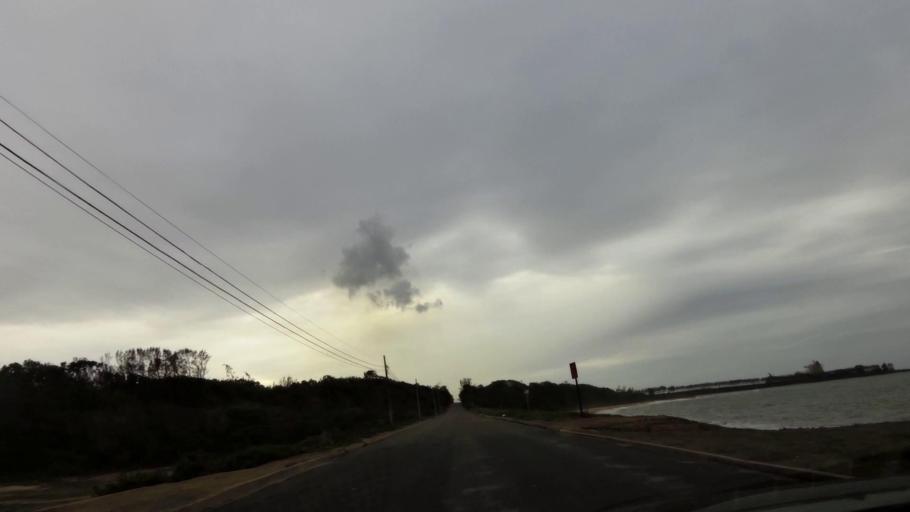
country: BR
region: Espirito Santo
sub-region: Piuma
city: Piuma
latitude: -20.7966
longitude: -40.5823
